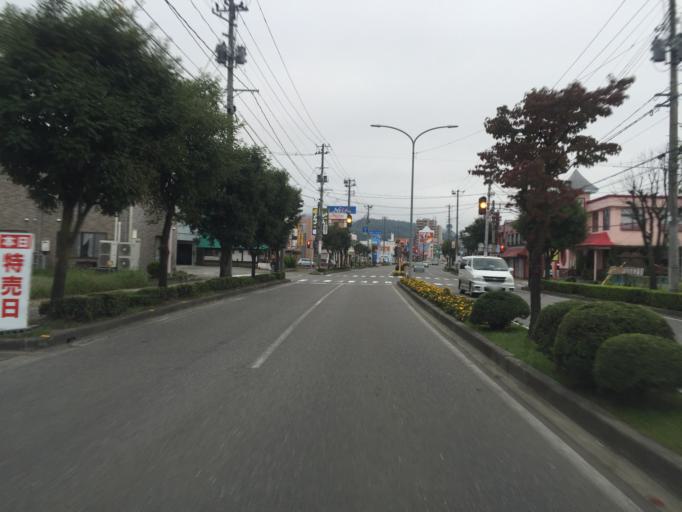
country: JP
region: Fukushima
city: Kitakata
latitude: 37.5001
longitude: 139.9432
